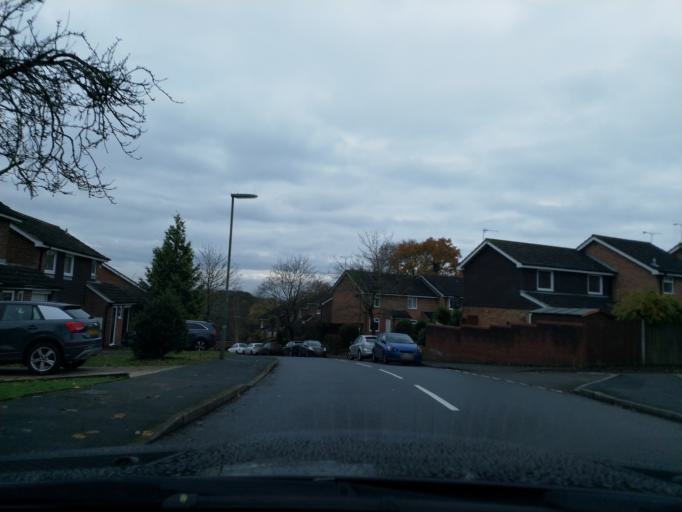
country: GB
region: England
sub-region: Surrey
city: Frimley
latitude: 51.3140
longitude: -0.7300
